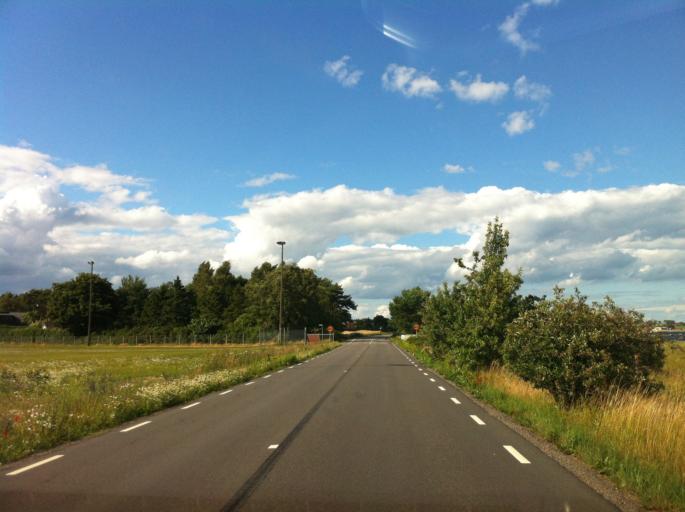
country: SE
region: Skane
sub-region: Simrishamns Kommun
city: Simrishamn
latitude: 55.4574
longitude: 14.2709
